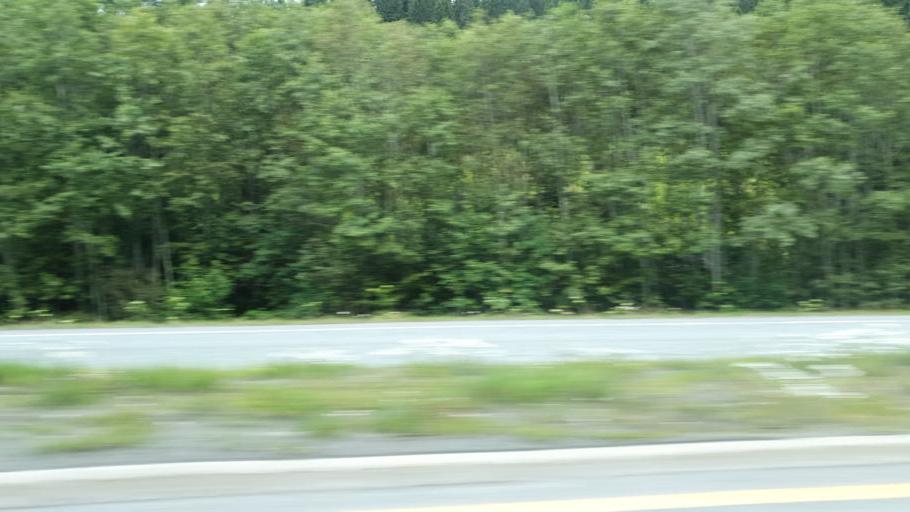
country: NO
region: Sor-Trondelag
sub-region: Midtre Gauldal
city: Storen
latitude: 63.0250
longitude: 10.2535
